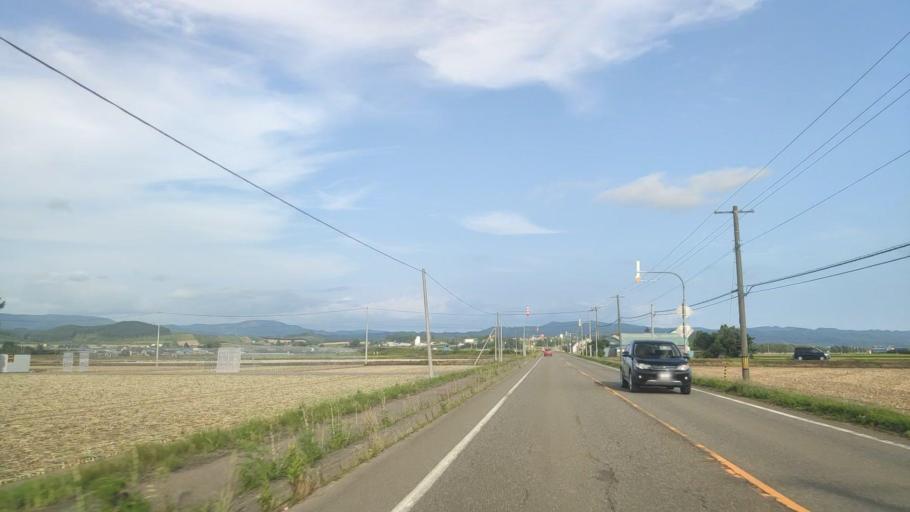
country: JP
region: Hokkaido
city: Iwamizawa
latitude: 43.0279
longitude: 141.8182
